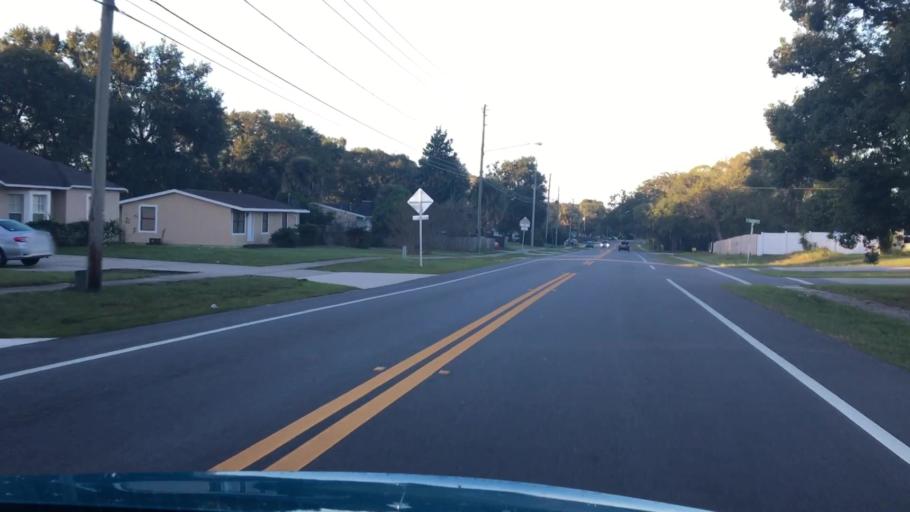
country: US
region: Florida
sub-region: Volusia County
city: Deltona
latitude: 28.8720
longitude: -81.2415
